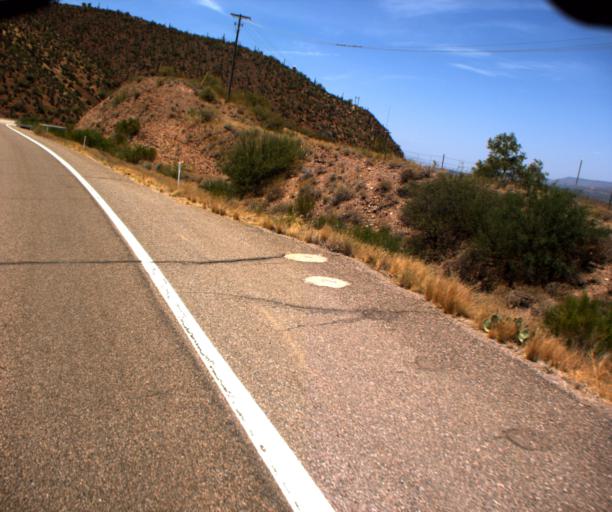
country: US
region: Arizona
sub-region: Gila County
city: Tonto Basin
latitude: 33.6690
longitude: -111.1411
